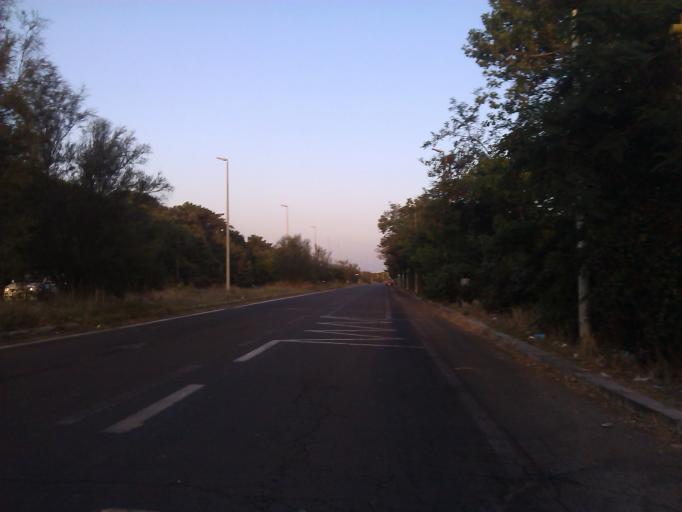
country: IT
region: Latium
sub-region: Citta metropolitana di Roma Capitale
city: Acilia-Castel Fusano-Ostia Antica
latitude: 41.7070
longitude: 12.3386
